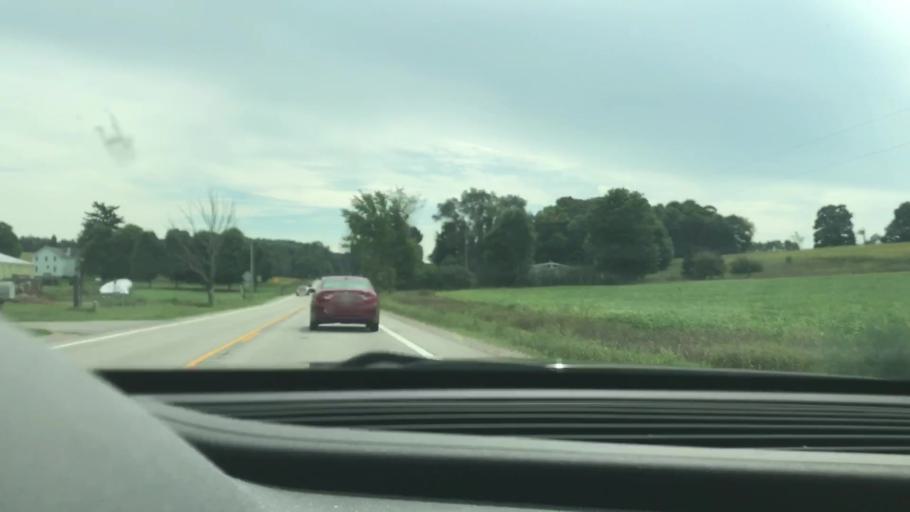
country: US
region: Michigan
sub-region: Antrim County
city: Bellaire
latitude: 45.0907
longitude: -85.2900
